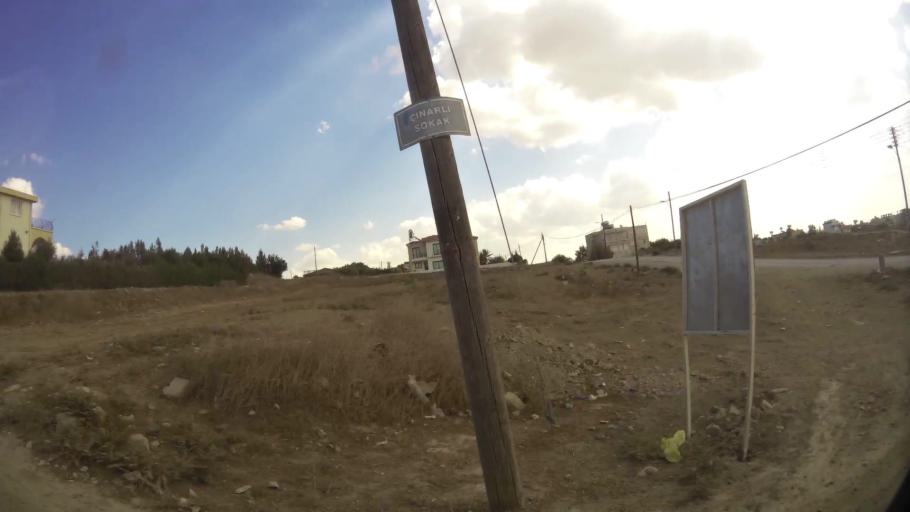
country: CY
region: Lefkosia
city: Nicosia
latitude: 35.2220
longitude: 33.3746
